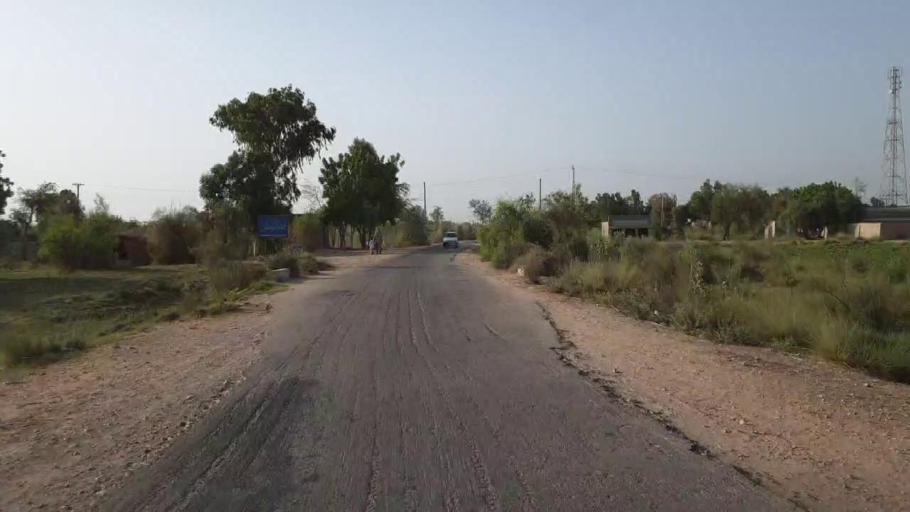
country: PK
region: Sindh
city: Jam Sahib
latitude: 26.4806
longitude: 68.8599
